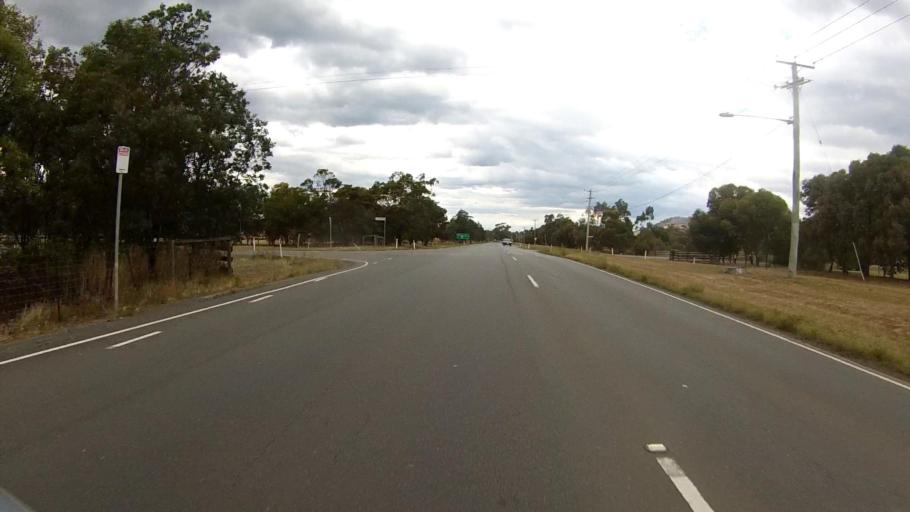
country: AU
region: Tasmania
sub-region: Clarence
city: Cambridge
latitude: -42.8432
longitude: 147.4737
